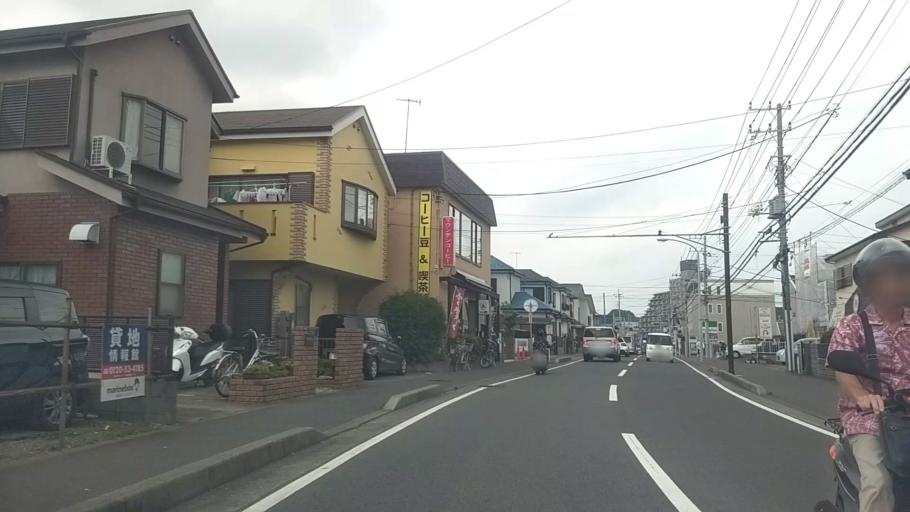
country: JP
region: Kanagawa
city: Fujisawa
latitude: 35.3420
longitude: 139.4372
